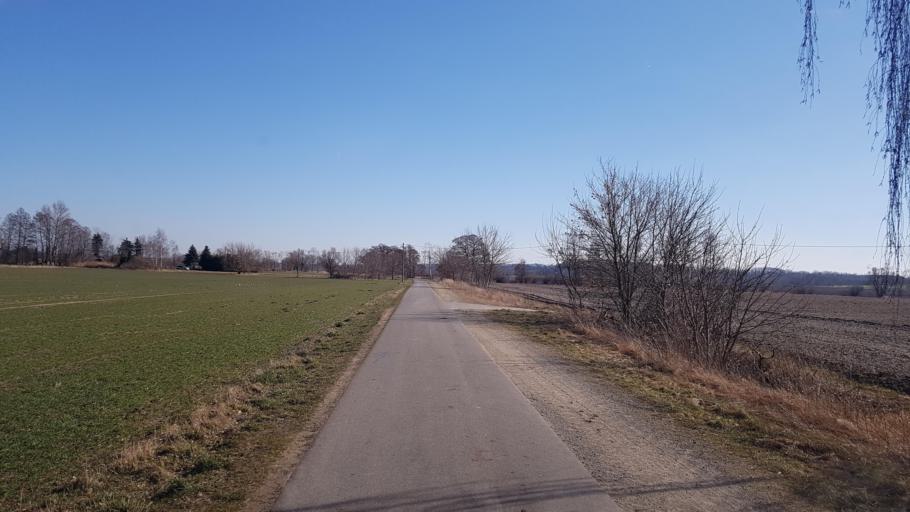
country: DE
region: Brandenburg
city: Hirschfeld
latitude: 51.3909
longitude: 13.6288
